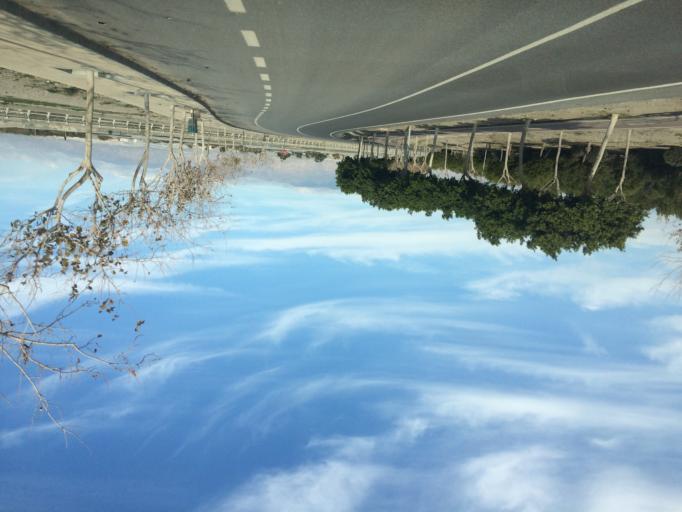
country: ES
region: Andalusia
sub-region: Provincia de Almeria
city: Almeria
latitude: 36.8280
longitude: -2.4282
